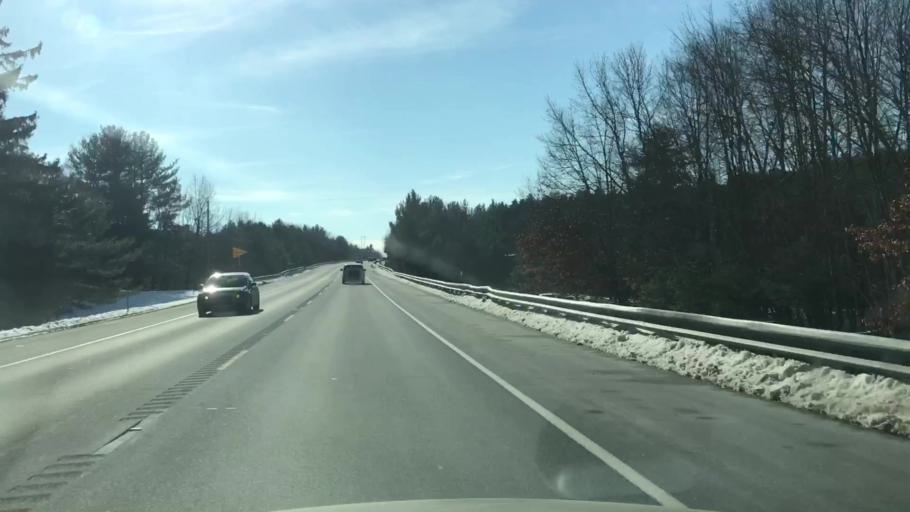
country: US
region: New Hampshire
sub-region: Hillsborough County
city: Milford
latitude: 42.8490
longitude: -71.6130
